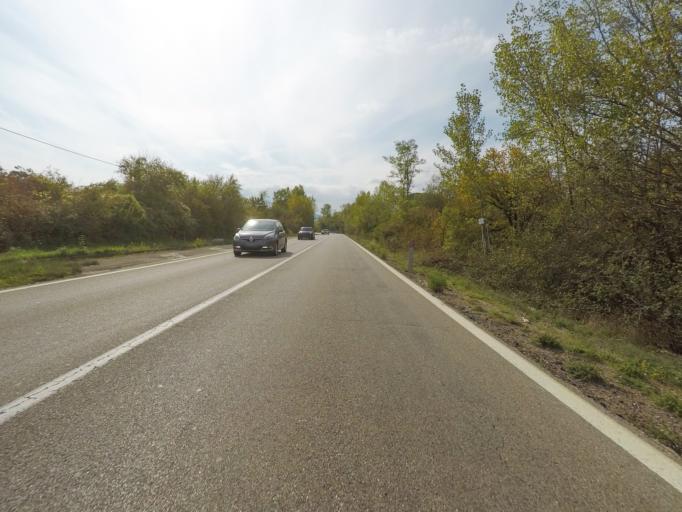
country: IT
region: Tuscany
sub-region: Provincia di Siena
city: Rosia
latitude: 43.2023
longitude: 11.2767
